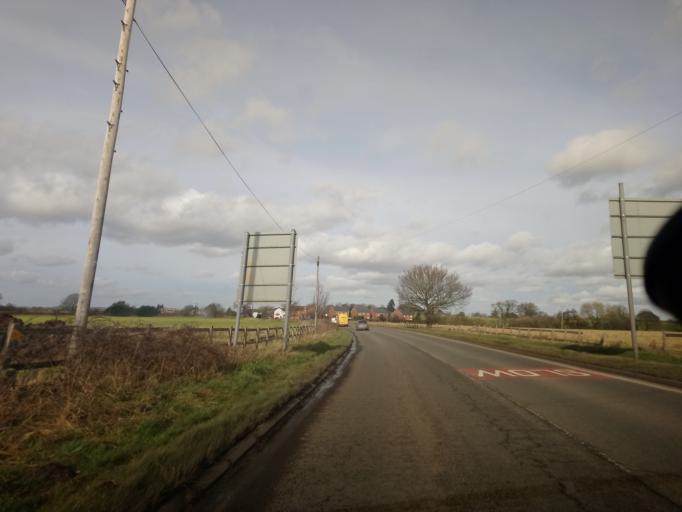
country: GB
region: England
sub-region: Telford and Wrekin
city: Eyton upon the Weald Moors
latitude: 52.7654
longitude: -2.5460
